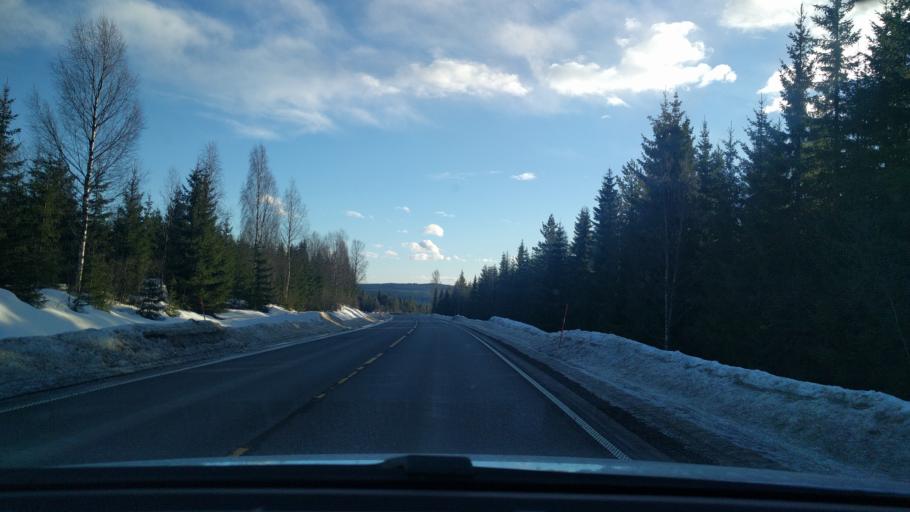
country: NO
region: Hedmark
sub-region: Trysil
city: Innbygda
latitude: 61.0986
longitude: 12.0041
